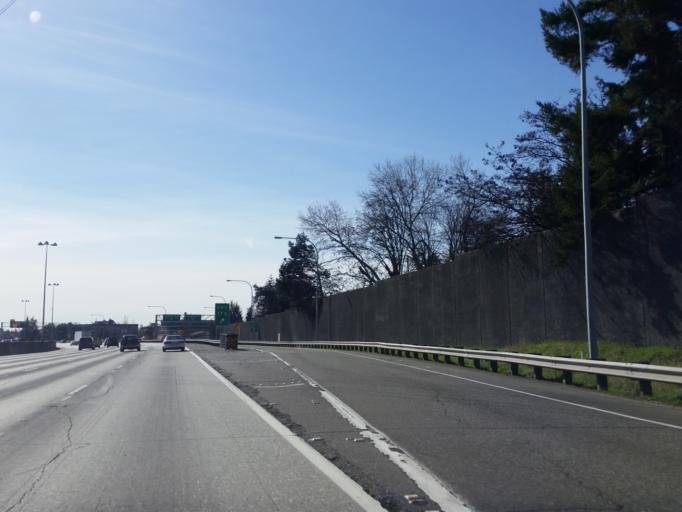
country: US
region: Washington
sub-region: King County
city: Shoreline
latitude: 47.7124
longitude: -122.3285
